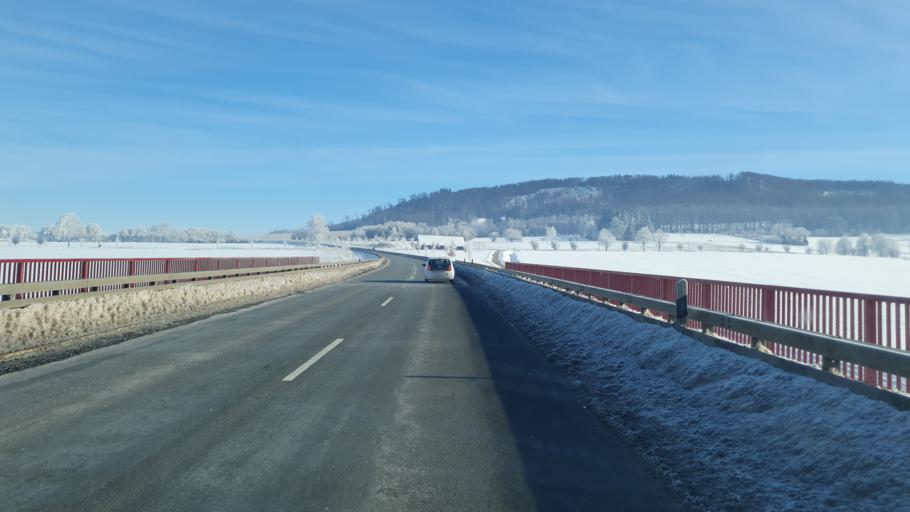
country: DE
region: Lower Saxony
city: Aerzen
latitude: 52.0376
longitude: 9.2634
